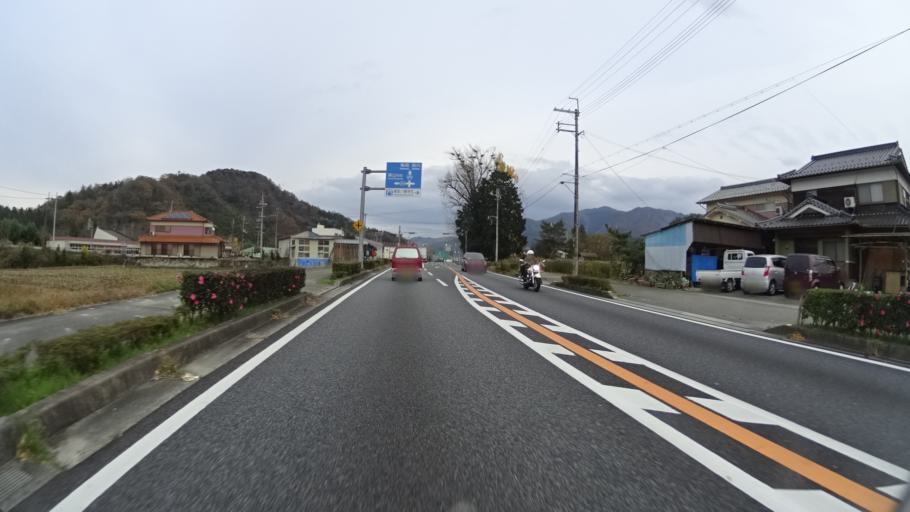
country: JP
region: Hyogo
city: Sasayama
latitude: 35.0702
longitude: 135.2773
